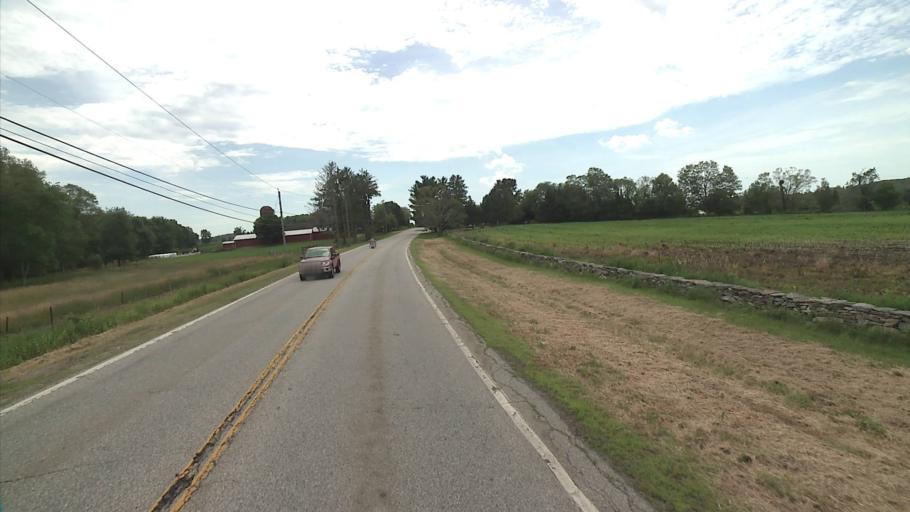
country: US
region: Connecticut
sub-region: New London County
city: Preston City
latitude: 41.5416
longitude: -71.9677
